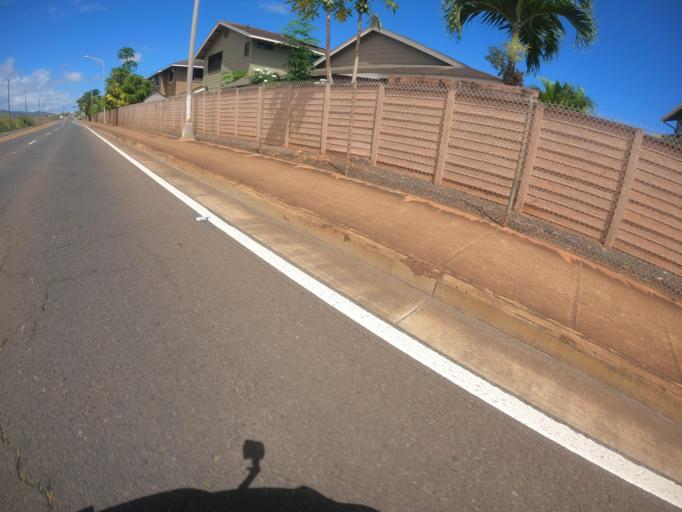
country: US
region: Hawaii
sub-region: Honolulu County
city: Village Park
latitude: 21.3940
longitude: -158.0368
